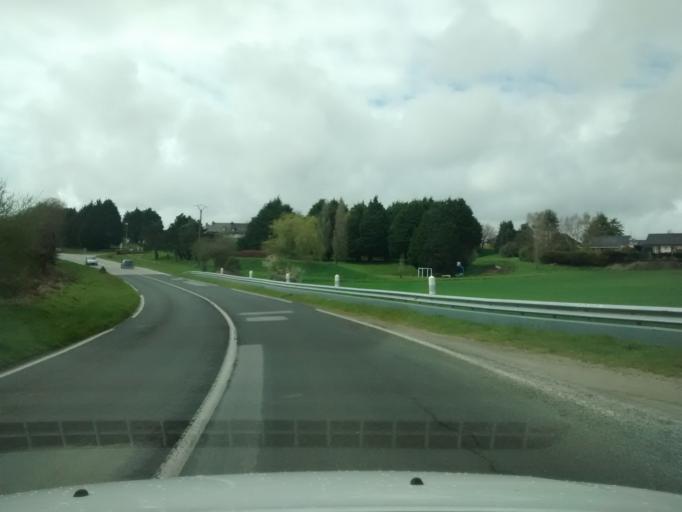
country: FR
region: Brittany
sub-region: Departement du Morbihan
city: Gestel
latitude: 47.7948
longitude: -3.4624
